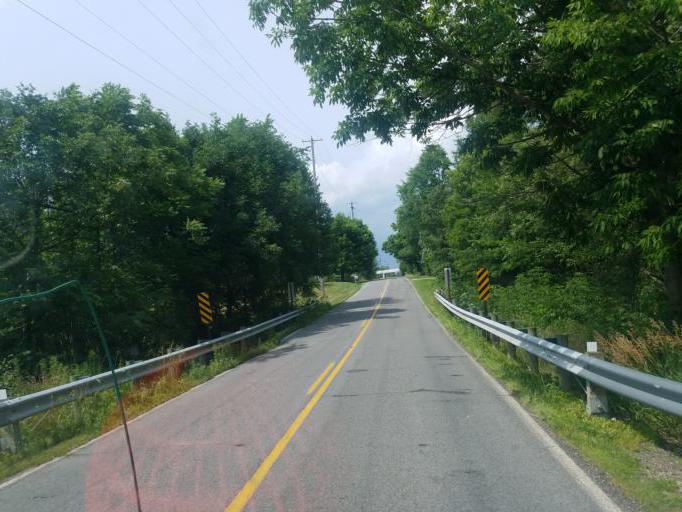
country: US
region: Ohio
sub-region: Portage County
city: Ravenna
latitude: 41.1041
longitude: -81.2204
